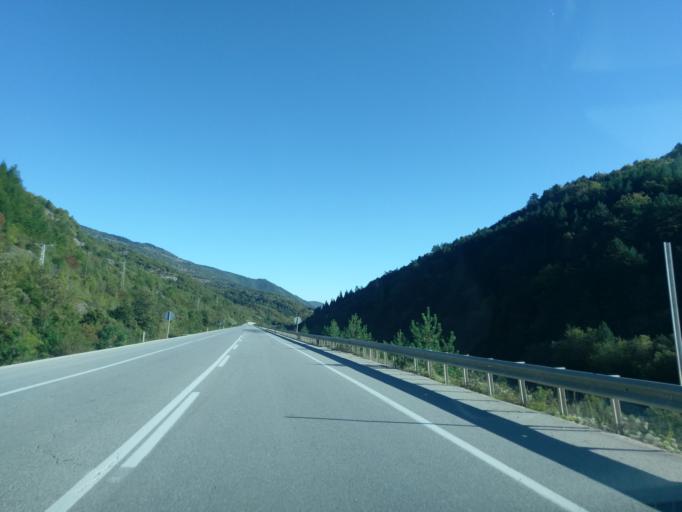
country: TR
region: Sinop
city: Erfelek
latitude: 41.7146
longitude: 34.9341
